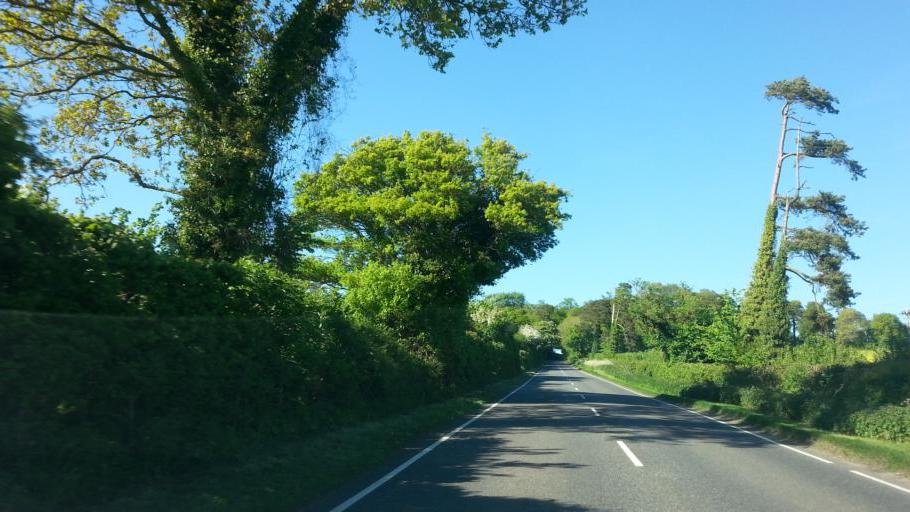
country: GB
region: England
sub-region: Somerset
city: Milborne Port
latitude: 50.9664
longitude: -2.4272
